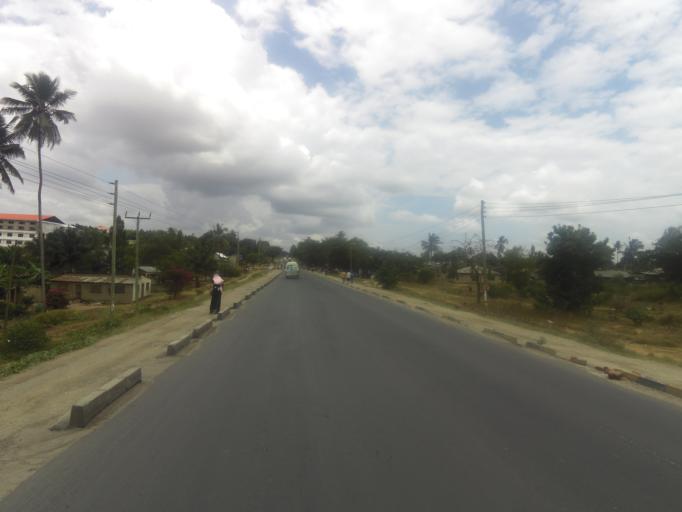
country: TZ
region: Pwani
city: Vikindu
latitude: -6.9554
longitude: 39.2833
